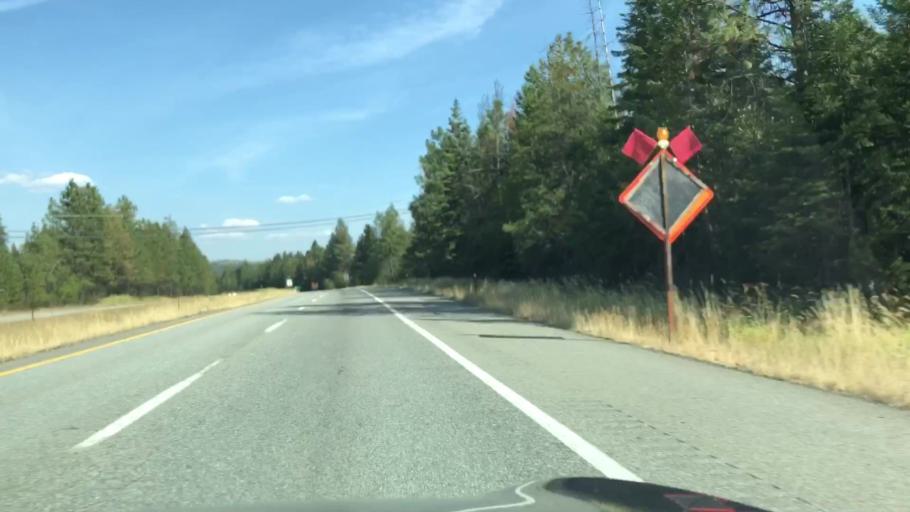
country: US
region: Idaho
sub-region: Shoshone County
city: Pinehurst
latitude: 47.5507
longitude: -116.3031
